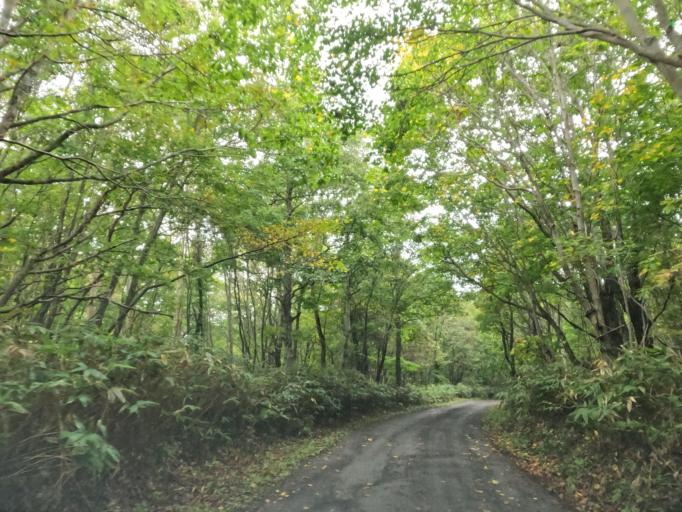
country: JP
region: Hokkaido
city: Date
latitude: 42.5002
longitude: 140.9234
